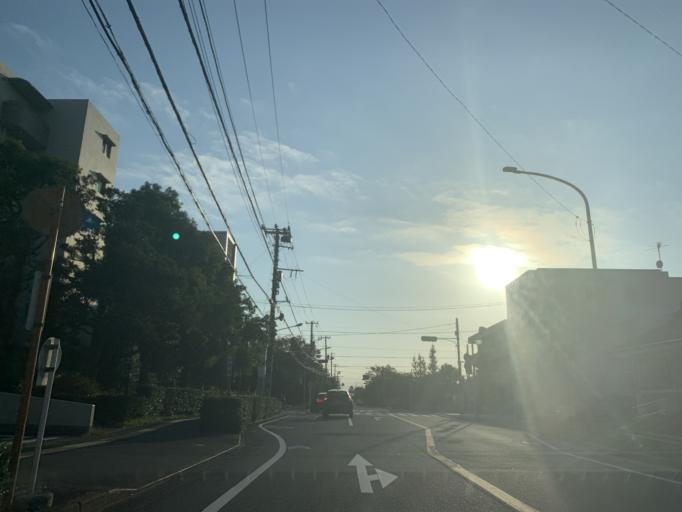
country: JP
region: Tokyo
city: Urayasu
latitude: 35.6513
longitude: 139.9091
